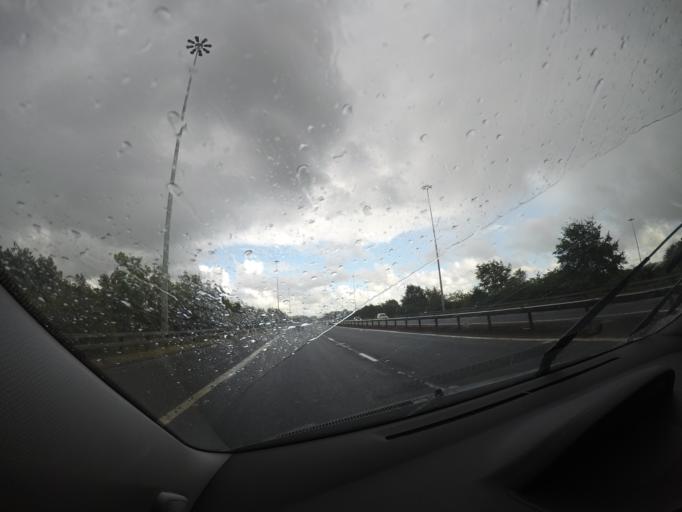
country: GB
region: Scotland
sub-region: South Lanarkshire
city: Hamilton
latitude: 55.7830
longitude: -4.0247
